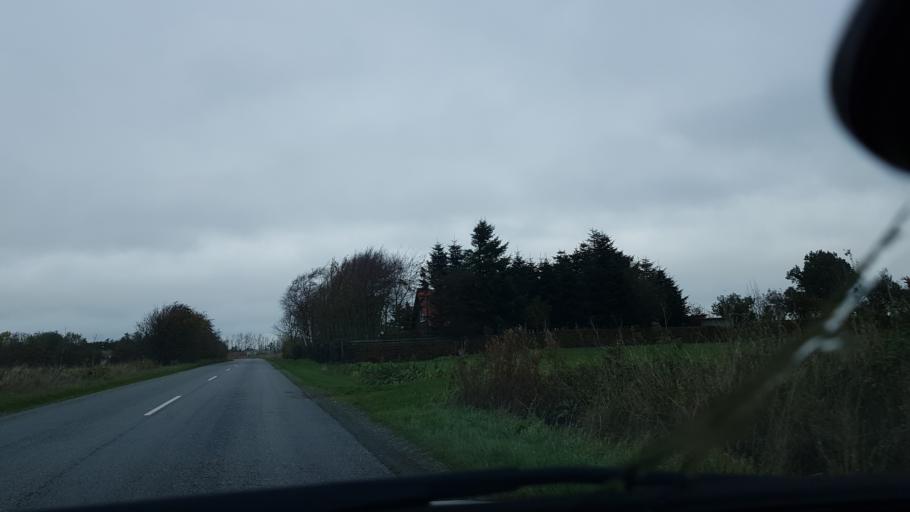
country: DK
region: South Denmark
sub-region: Tonder Kommune
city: Sherrebek
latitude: 55.2292
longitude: 8.8354
